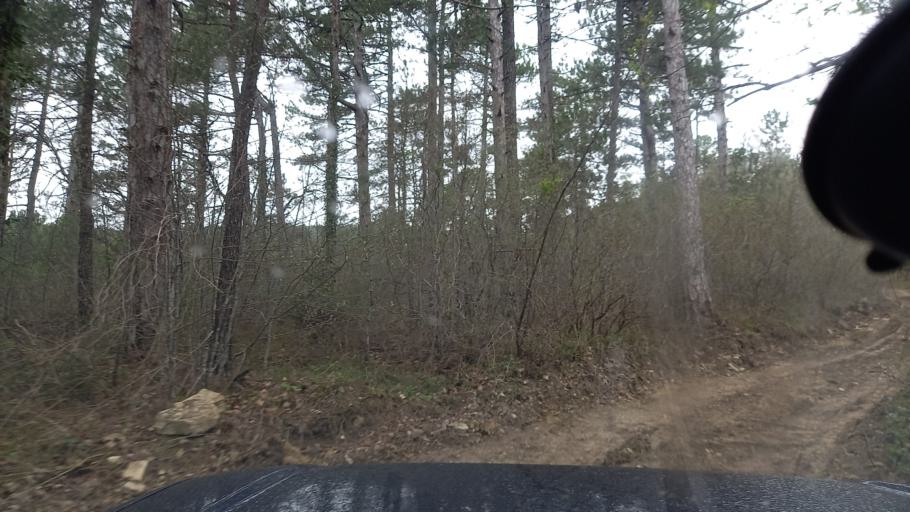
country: RU
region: Krasnodarskiy
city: Arkhipo-Osipovka
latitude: 44.3708
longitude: 38.4725
